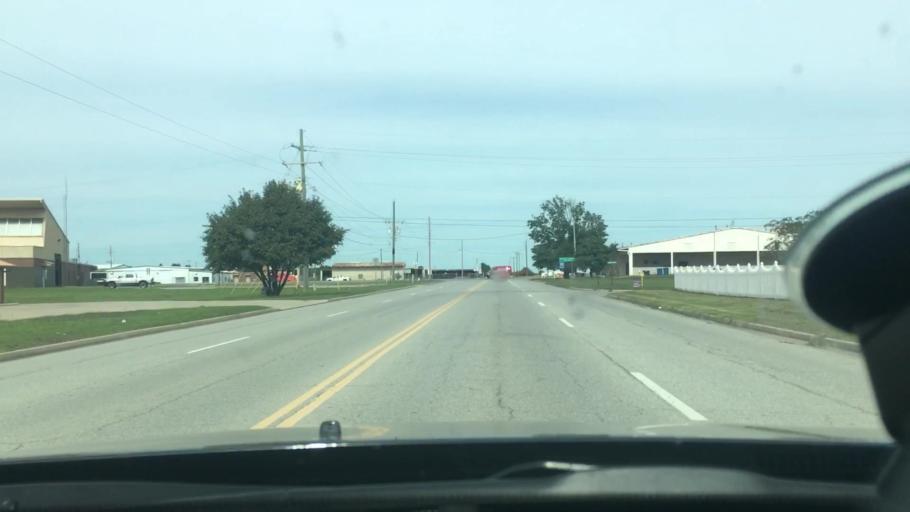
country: US
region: Oklahoma
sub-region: Atoka County
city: Atoka
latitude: 34.3923
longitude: -96.1455
